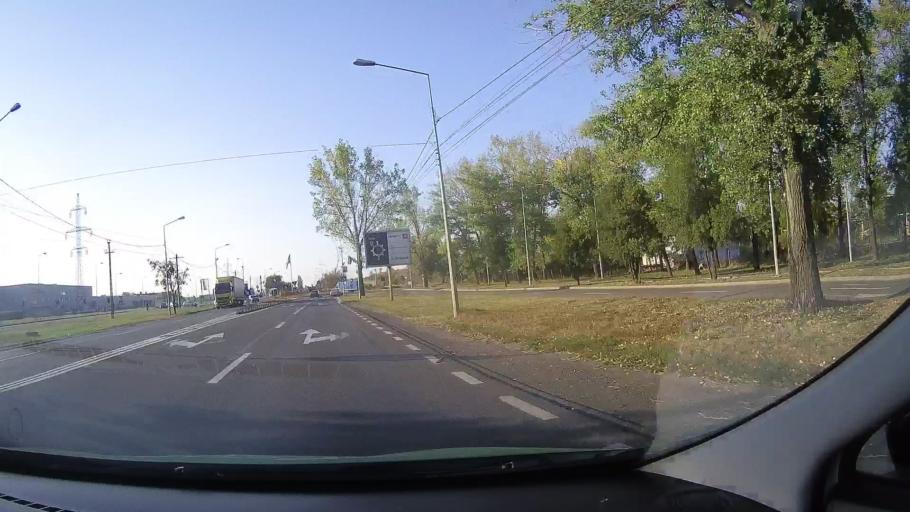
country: RO
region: Bihor
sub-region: Comuna Santandrei
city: Santandrei
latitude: 47.0874
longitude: 21.8791
